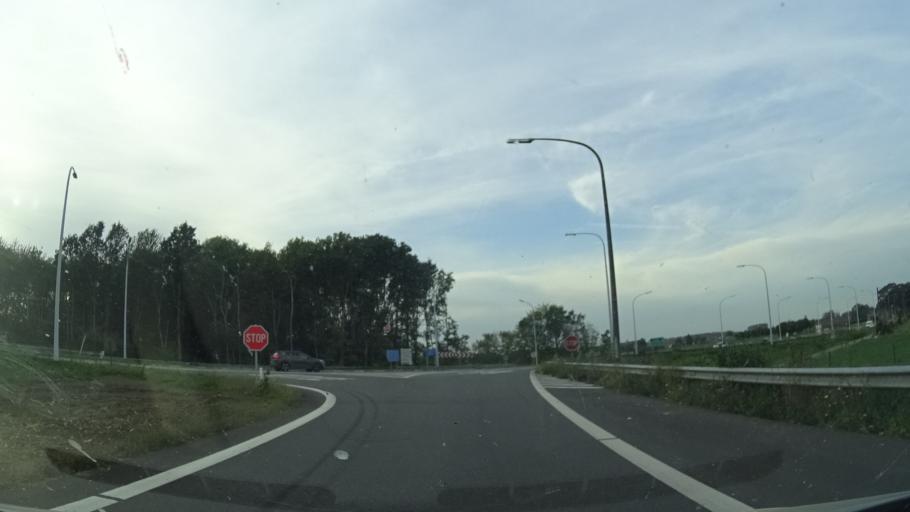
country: BE
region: Wallonia
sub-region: Province du Hainaut
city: Peruwelz
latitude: 50.5351
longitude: 3.6033
